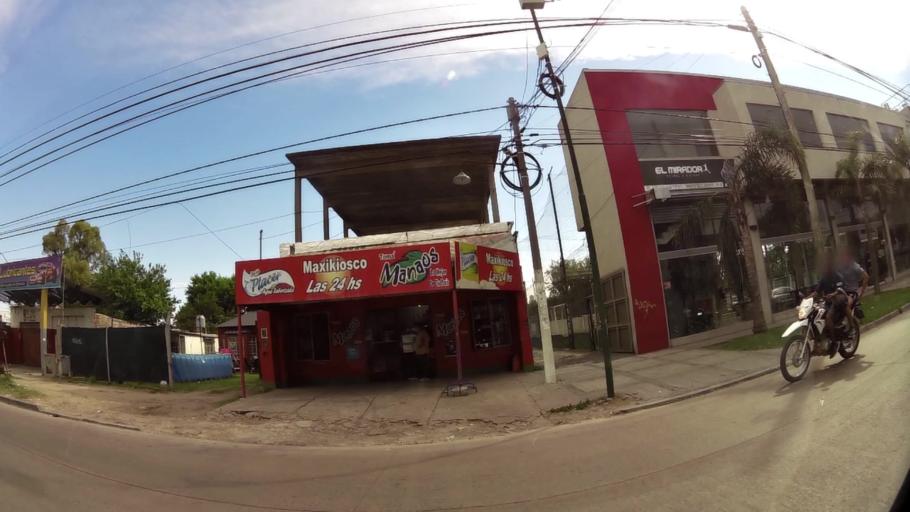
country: AR
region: Buenos Aires
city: Ituzaingo
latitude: -34.6503
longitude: -58.6841
